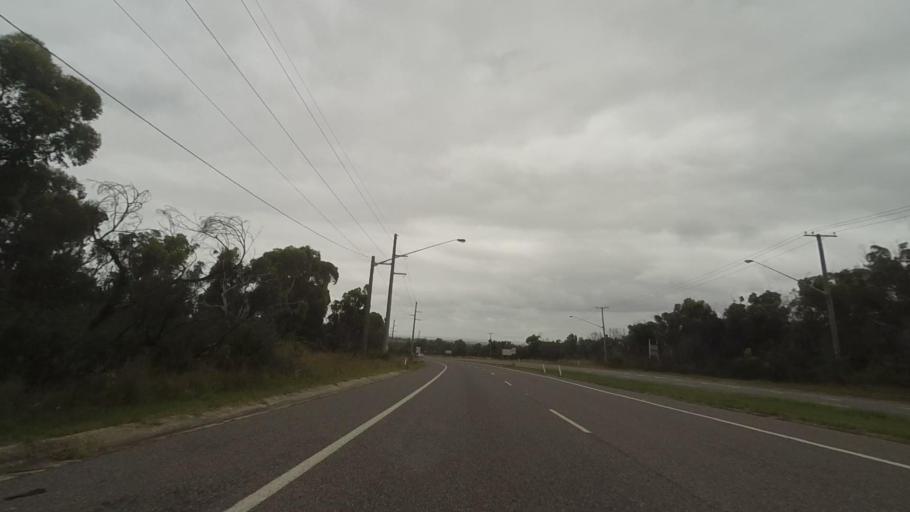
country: AU
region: New South Wales
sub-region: Wyong Shire
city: Kingfisher Shores
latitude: -33.1818
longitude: 151.5940
